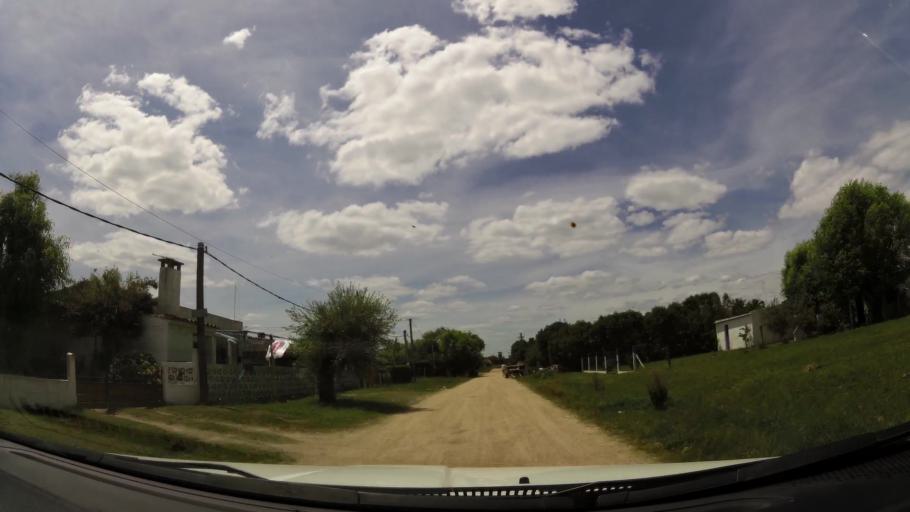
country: UY
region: San Jose
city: Delta del Tigre
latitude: -34.7528
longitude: -56.4239
